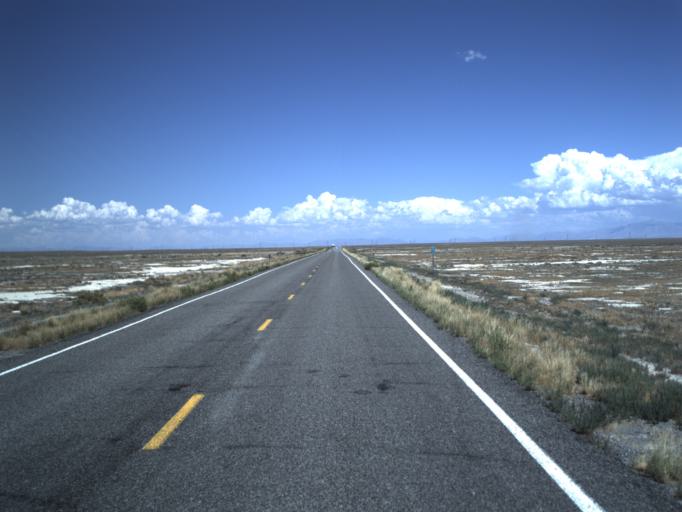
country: US
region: Utah
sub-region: Millard County
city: Delta
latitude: 39.2055
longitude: -112.9745
